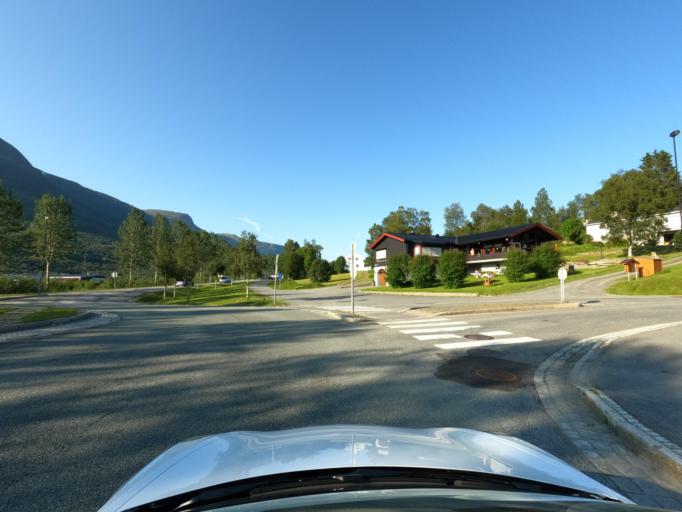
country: NO
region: Nordland
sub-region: Narvik
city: Bjerkvik
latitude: 68.5539
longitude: 17.5583
